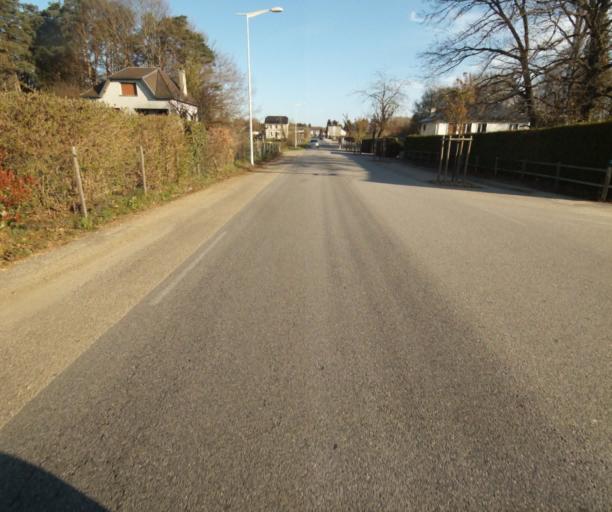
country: FR
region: Limousin
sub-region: Departement de la Correze
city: Correze
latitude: 45.3359
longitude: 1.8771
